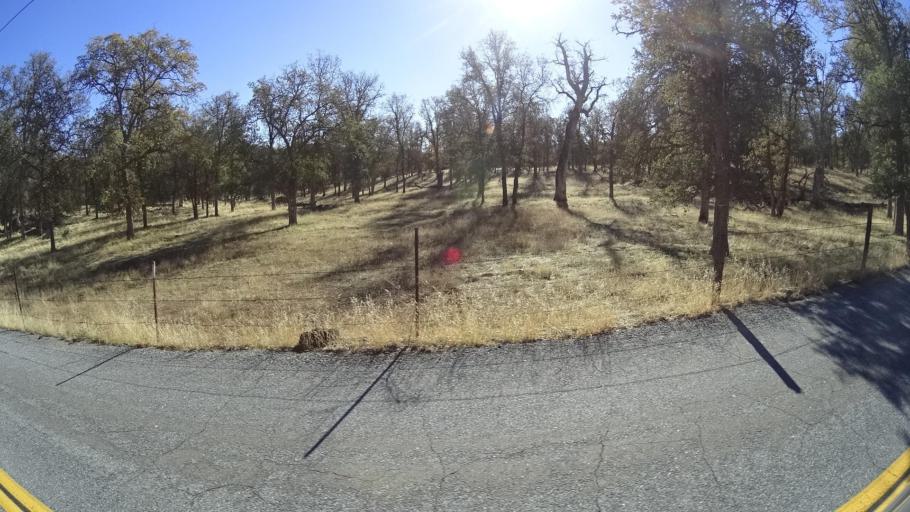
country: US
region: California
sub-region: Kern County
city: Alta Sierra
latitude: 35.7960
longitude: -118.7191
